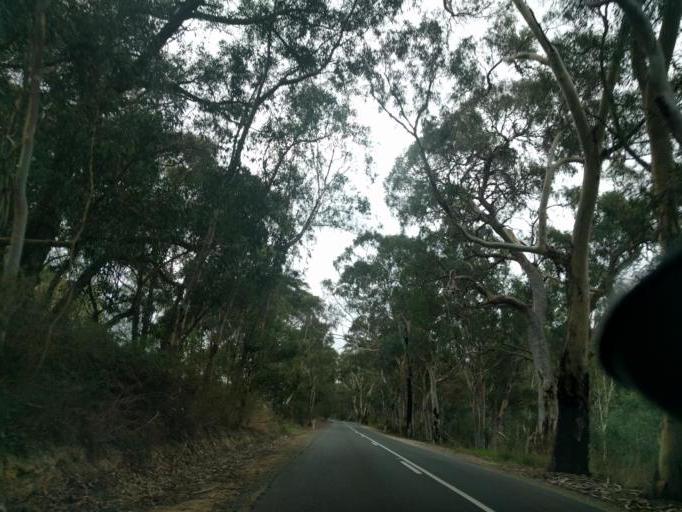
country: AU
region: South Australia
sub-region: Mount Barker
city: Hahndorf
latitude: -35.0657
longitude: 138.7718
